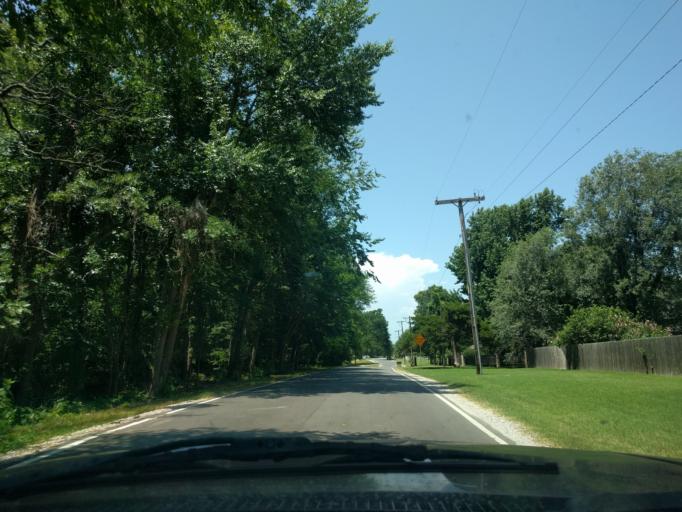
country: US
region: Oklahoma
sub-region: Tulsa County
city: Jenks
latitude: 36.0029
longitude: -95.9299
